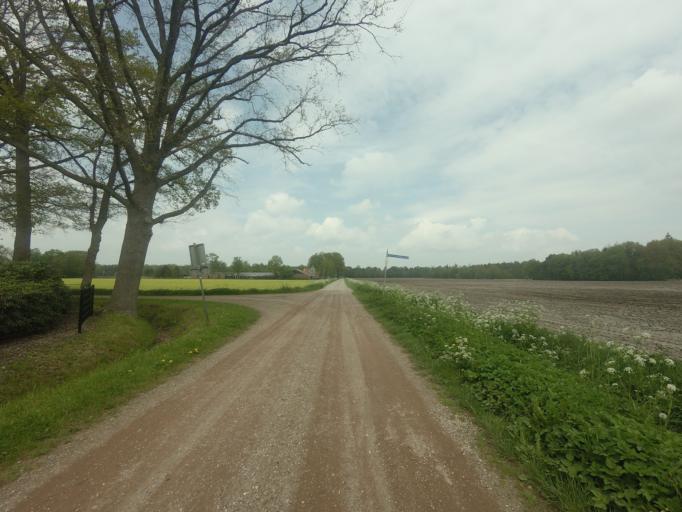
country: NL
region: Overijssel
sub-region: Gemeente Hof van Twente
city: Delden
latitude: 52.2328
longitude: 6.7258
